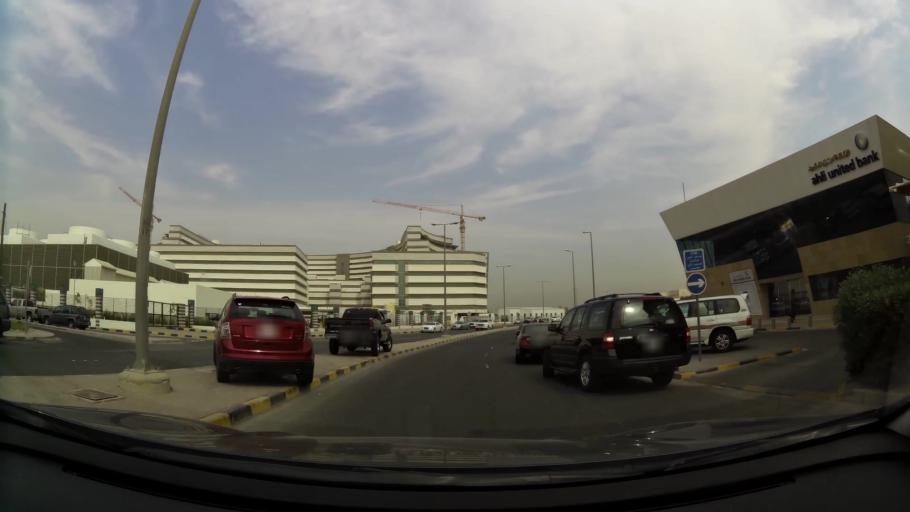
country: KW
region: Al Farwaniyah
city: Janub as Surrah
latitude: 29.2731
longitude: 48.0162
